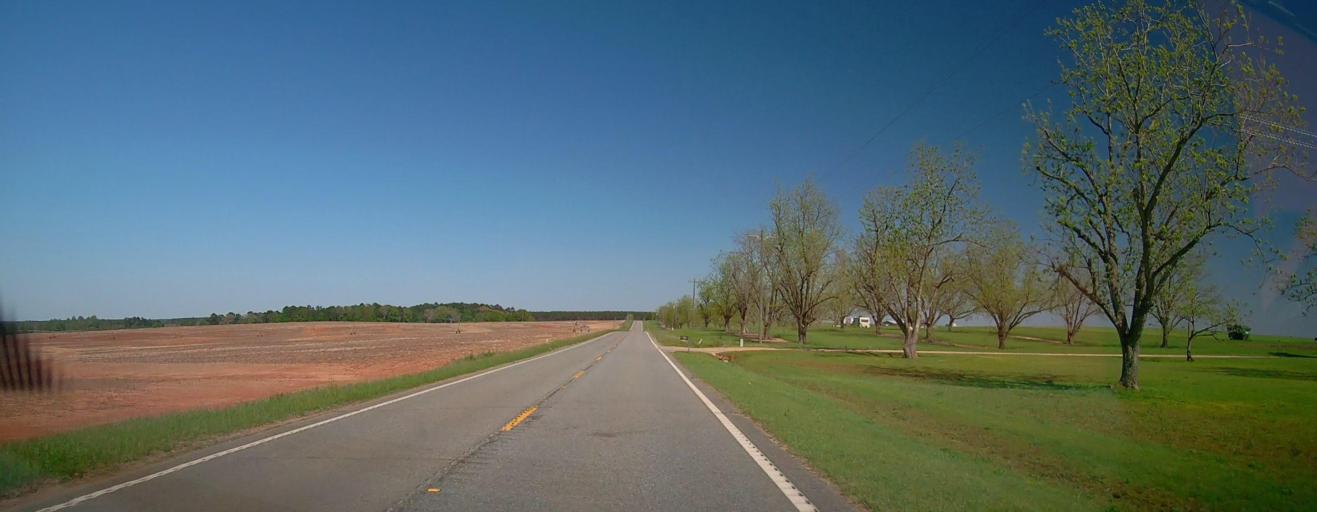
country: US
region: Georgia
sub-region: Dooly County
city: Unadilla
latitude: 32.2599
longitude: -83.6694
